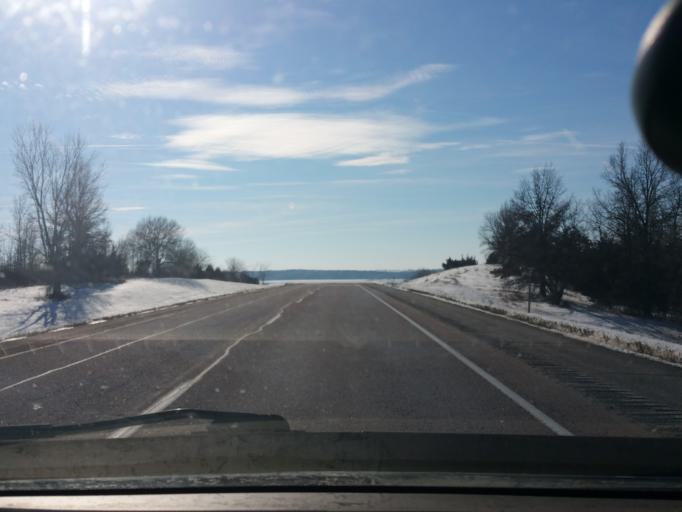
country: US
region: Iowa
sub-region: Decatur County
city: Leon
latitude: 40.6907
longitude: -93.8462
